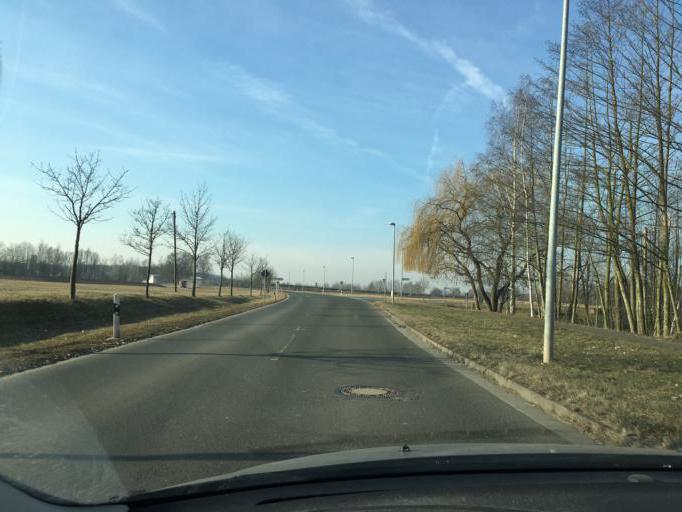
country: DE
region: Thuringia
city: Nobitz
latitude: 50.9755
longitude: 12.5186
